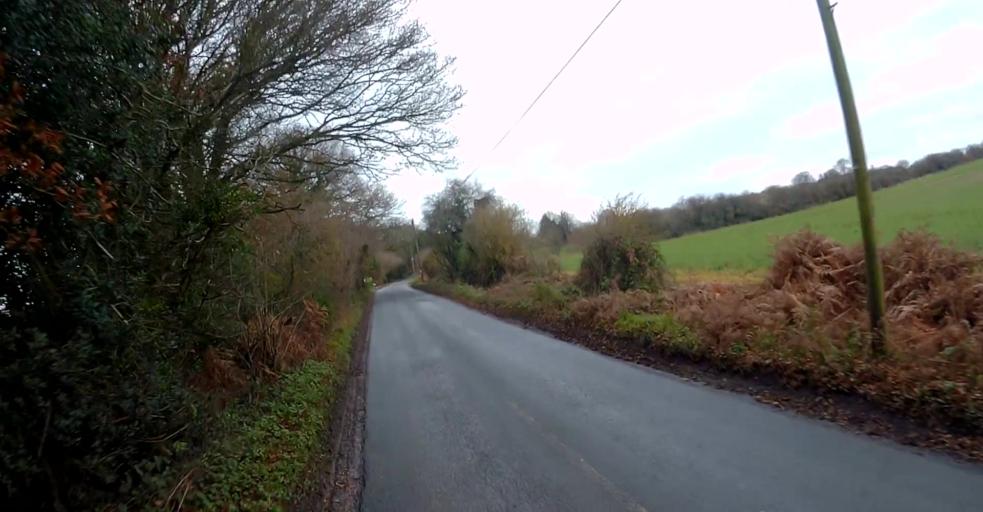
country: GB
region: England
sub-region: Hampshire
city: Basingstoke
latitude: 51.1904
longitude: -1.1566
